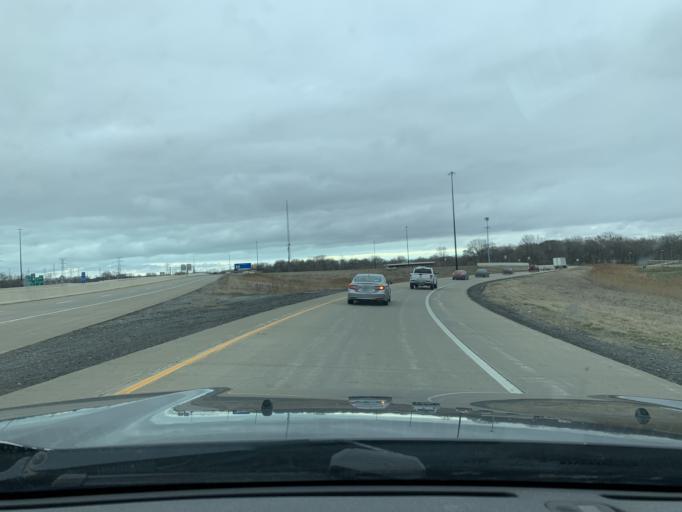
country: US
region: Indiana
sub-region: Lake County
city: New Chicago
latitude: 41.5666
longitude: -87.3027
